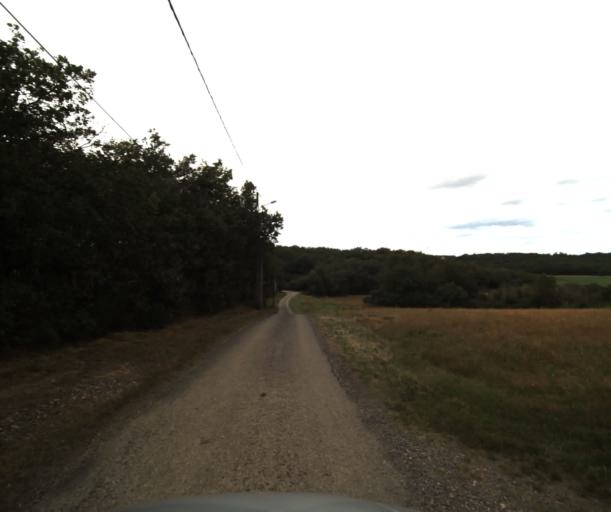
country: FR
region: Midi-Pyrenees
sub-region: Departement de la Haute-Garonne
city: Le Fauga
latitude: 43.4123
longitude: 1.3227
